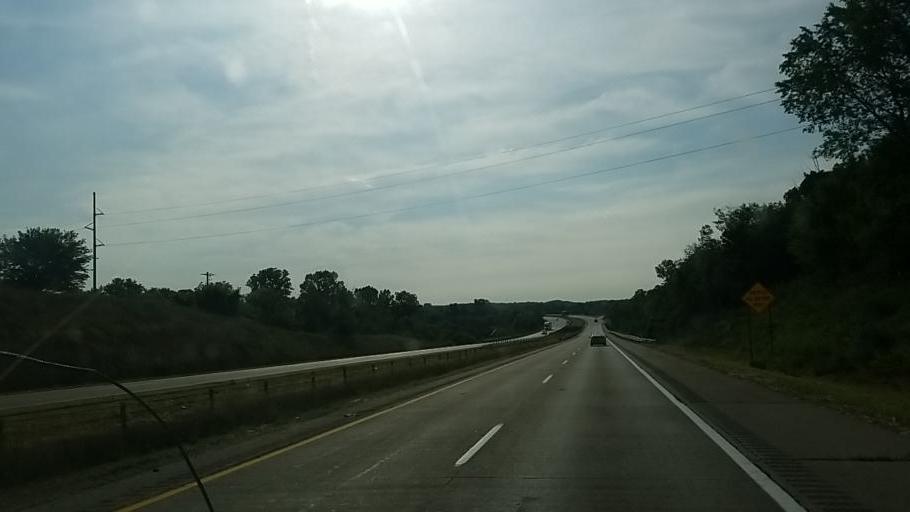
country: US
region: Michigan
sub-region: Ionia County
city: Portland
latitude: 42.8616
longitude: -84.9216
